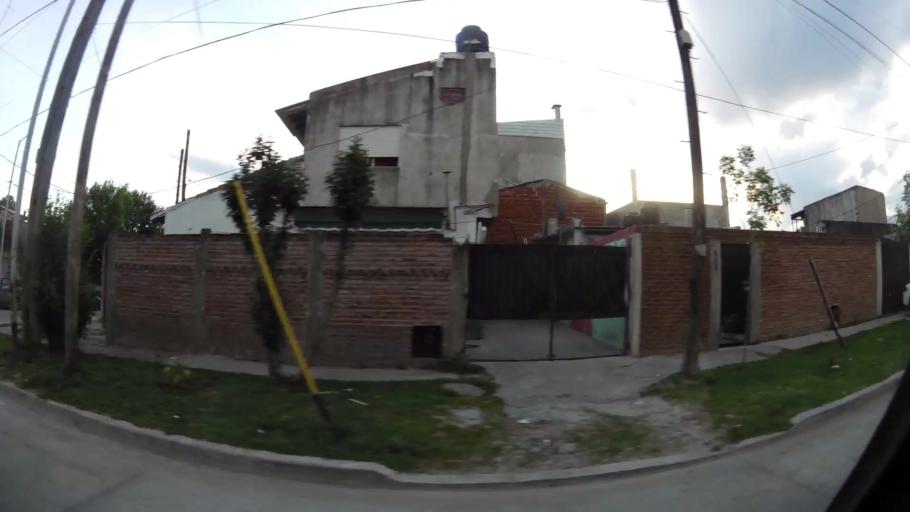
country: AR
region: Buenos Aires
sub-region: Partido de Avellaneda
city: Avellaneda
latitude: -34.6817
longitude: -58.3260
